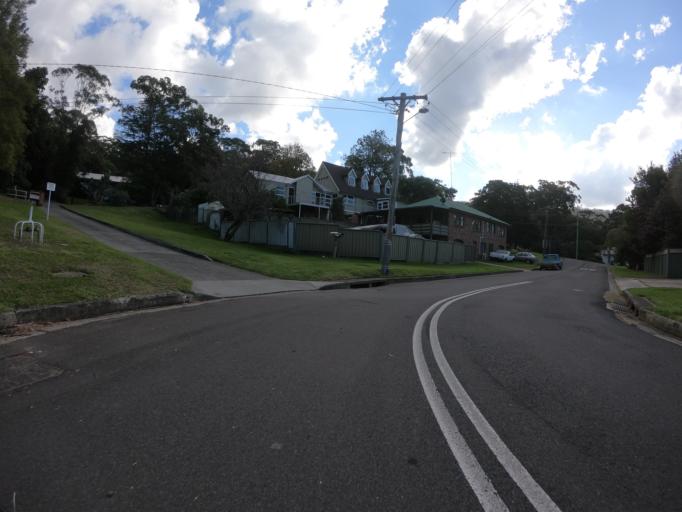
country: AU
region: New South Wales
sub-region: Wollongong
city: Cordeaux Heights
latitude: -34.4334
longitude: 150.8132
